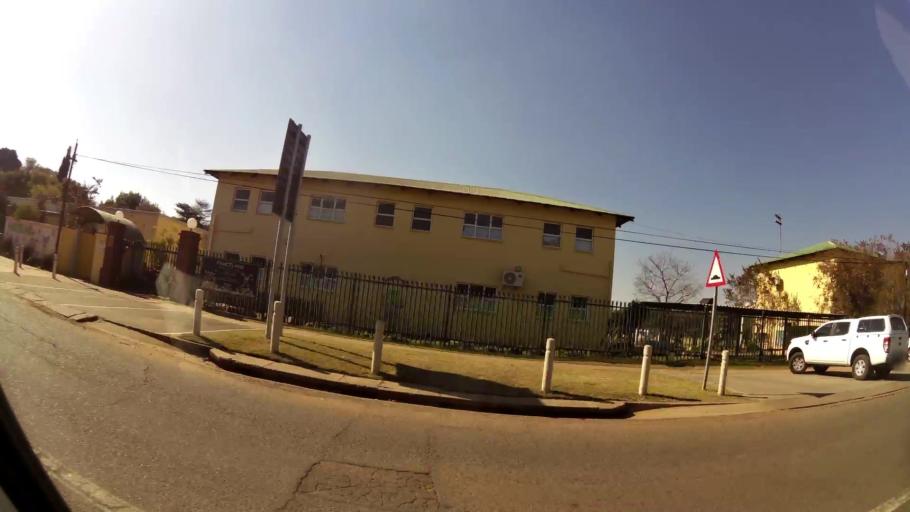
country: ZA
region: Gauteng
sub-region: City of Tshwane Metropolitan Municipality
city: Pretoria
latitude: -25.7667
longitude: 28.2537
